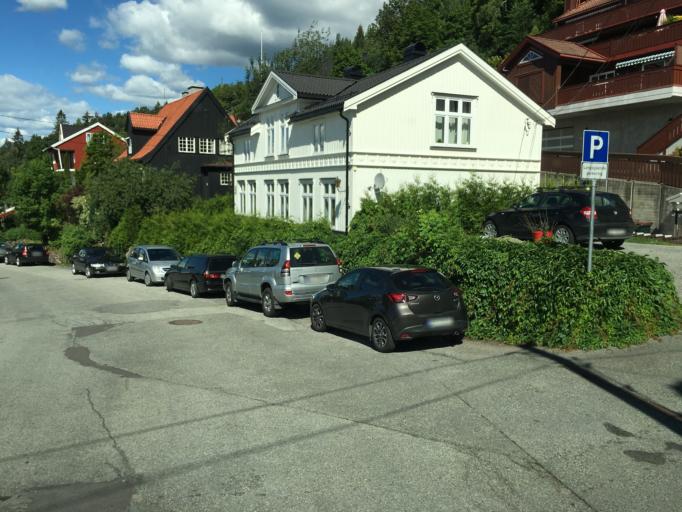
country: NO
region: Buskerud
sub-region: Drammen
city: Drammen
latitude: 59.7495
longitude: 10.2008
